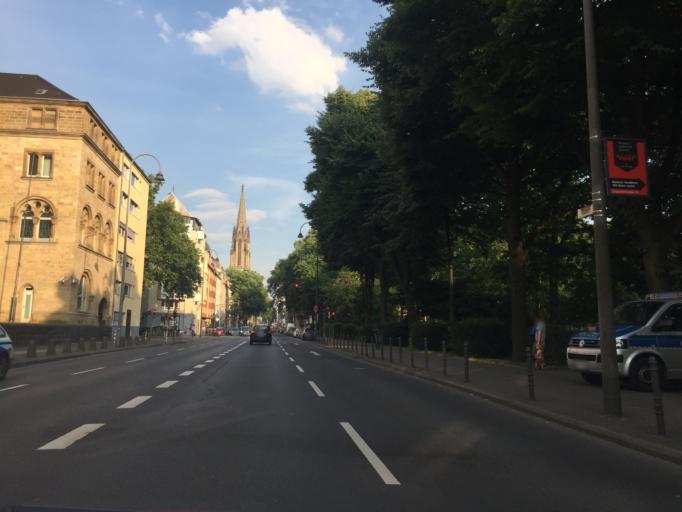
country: DE
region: North Rhine-Westphalia
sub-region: Regierungsbezirk Koln
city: Neustadt/Sued
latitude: 50.9321
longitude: 6.9360
